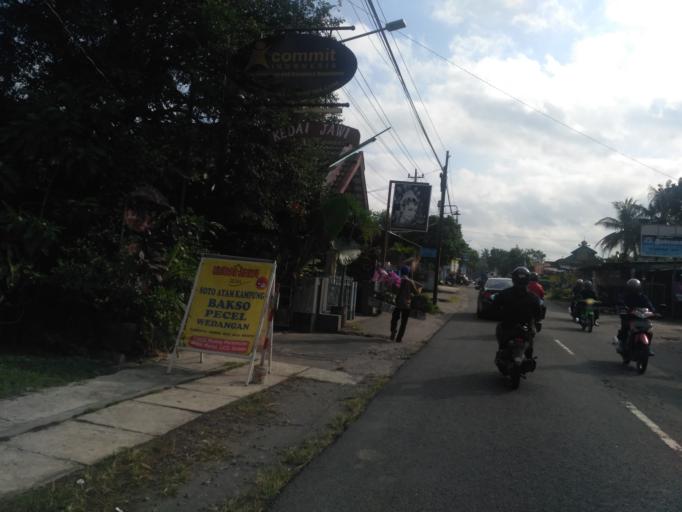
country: ID
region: Daerah Istimewa Yogyakarta
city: Melati
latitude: -7.7548
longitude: 110.3470
